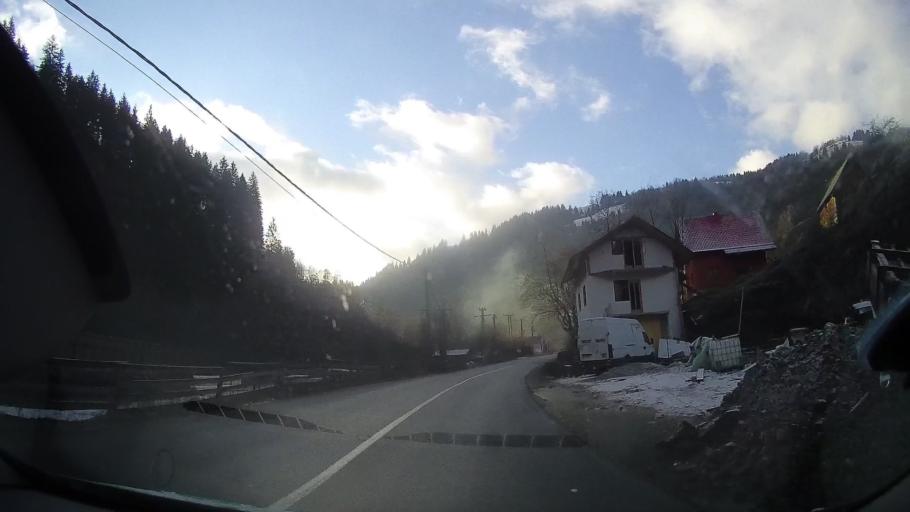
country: RO
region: Alba
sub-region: Comuna Vadu Motilor
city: Vadu Motilor
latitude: 46.4275
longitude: 22.9639
